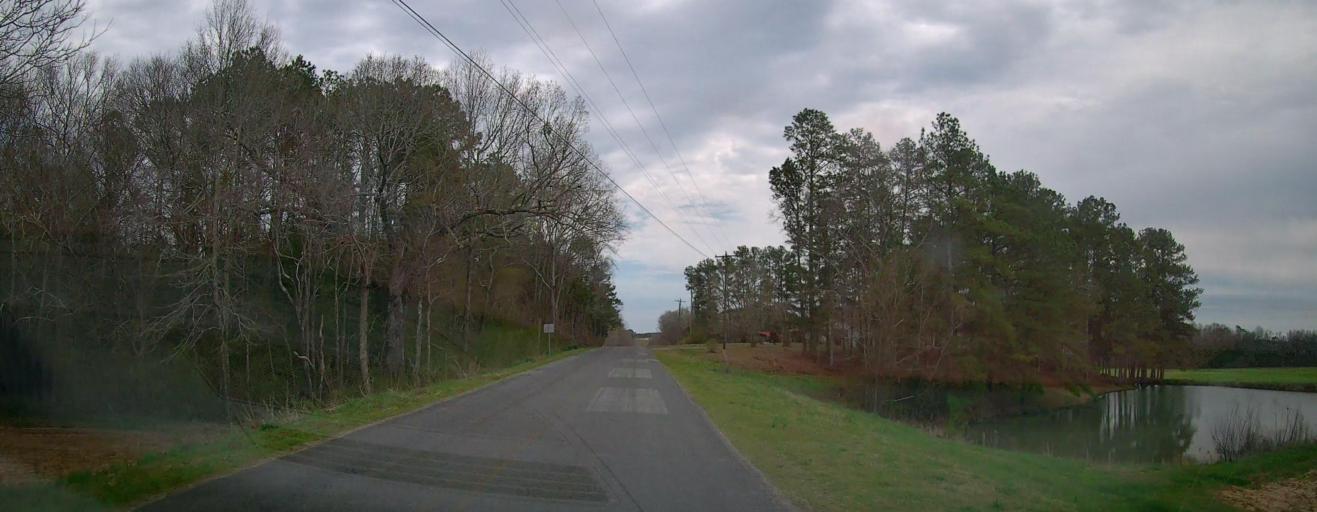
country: US
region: Alabama
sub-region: Marion County
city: Hamilton
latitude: 34.1893
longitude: -88.1465
